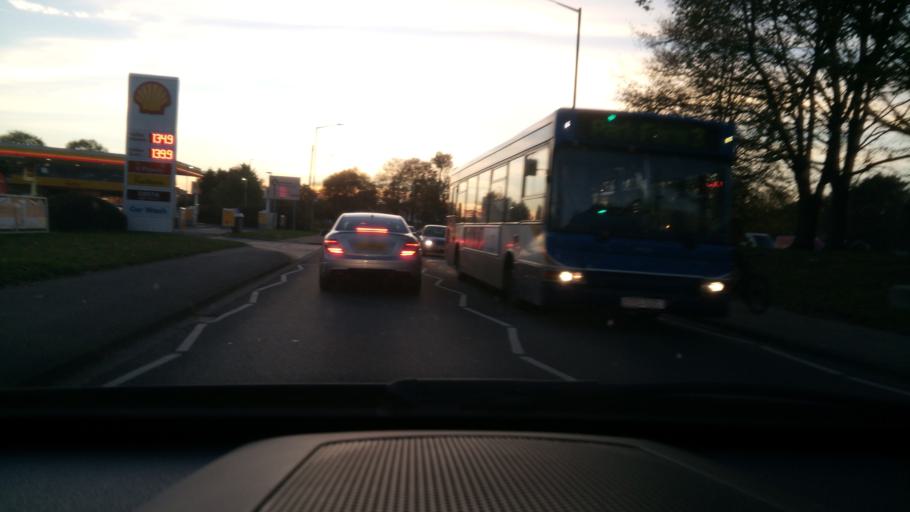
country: GB
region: England
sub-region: Peterborough
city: Peterborough
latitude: 52.5827
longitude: -0.2633
